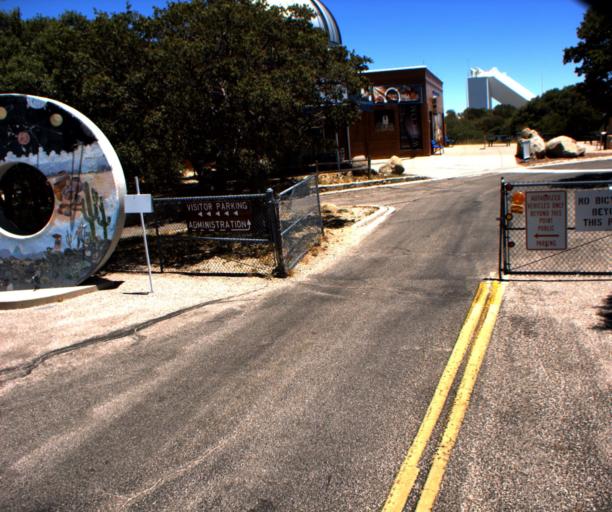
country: US
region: Arizona
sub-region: Pima County
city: Sells
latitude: 31.9602
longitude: -111.5985
